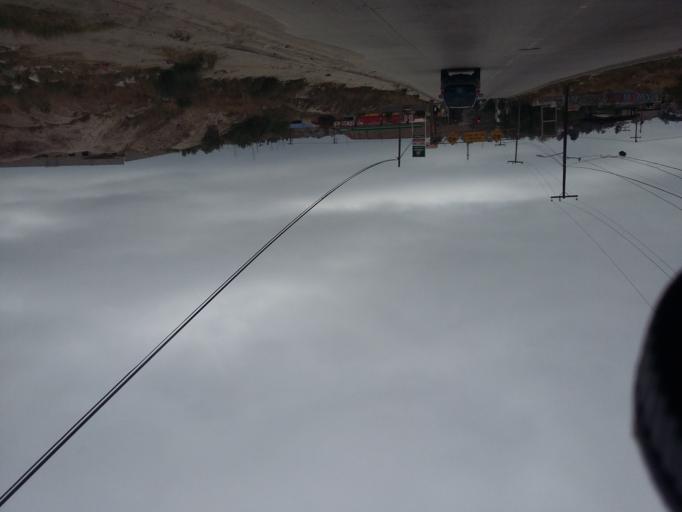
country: MX
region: Baja California
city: Tijuana
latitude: 32.5196
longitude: -116.9250
